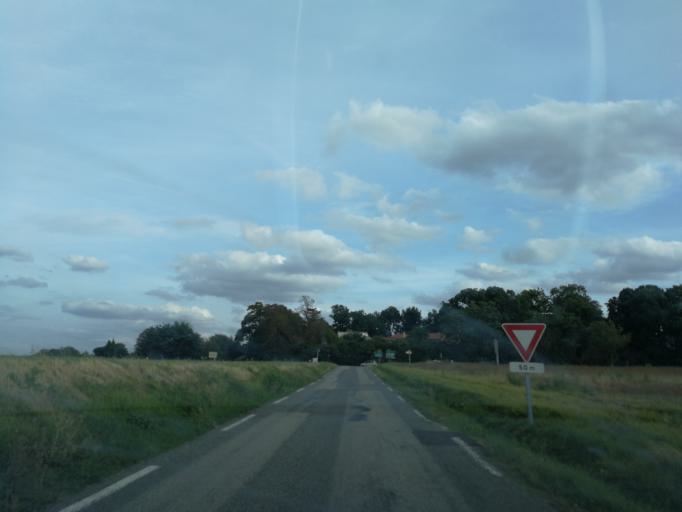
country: FR
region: Midi-Pyrenees
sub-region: Departement de la Haute-Garonne
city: Flourens
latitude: 43.5889
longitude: 1.5808
